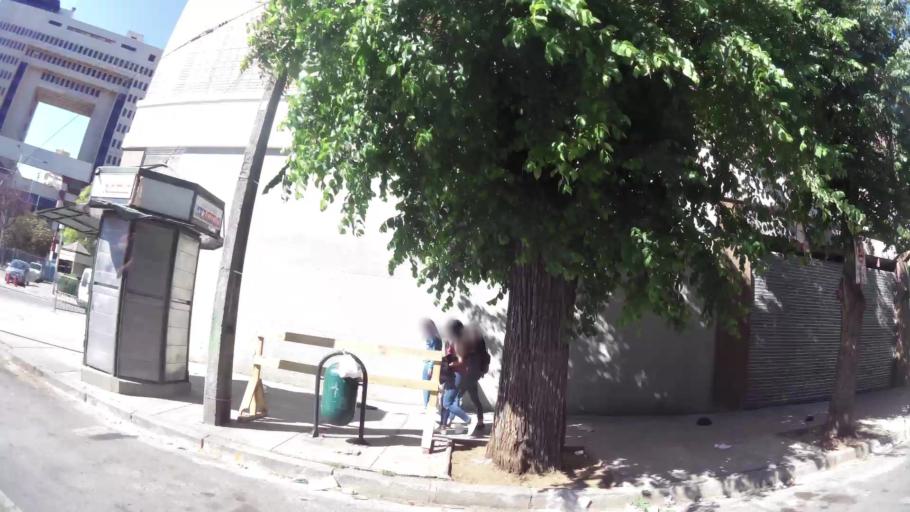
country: CL
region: Valparaiso
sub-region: Provincia de Valparaiso
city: Valparaiso
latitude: -33.0492
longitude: -71.6053
